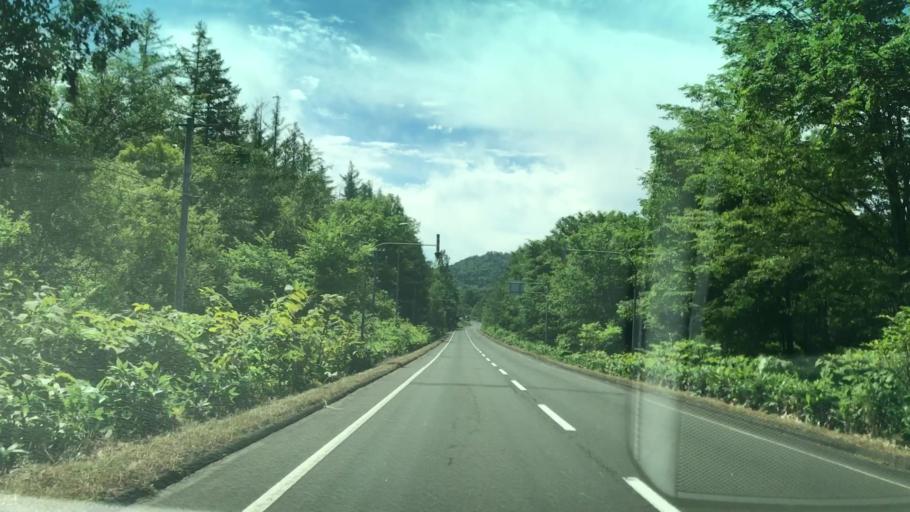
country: JP
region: Hokkaido
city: Shimo-furano
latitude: 42.9637
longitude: 142.4279
